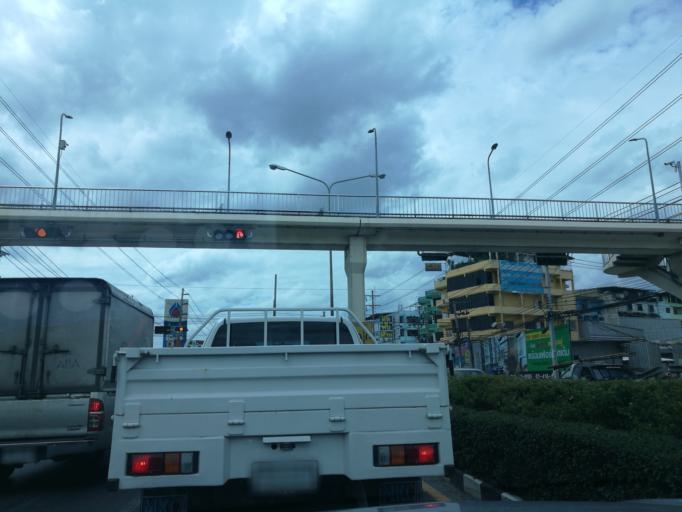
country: TH
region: Bangkok
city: Bang Khun Thian
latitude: 13.6613
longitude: 100.4294
